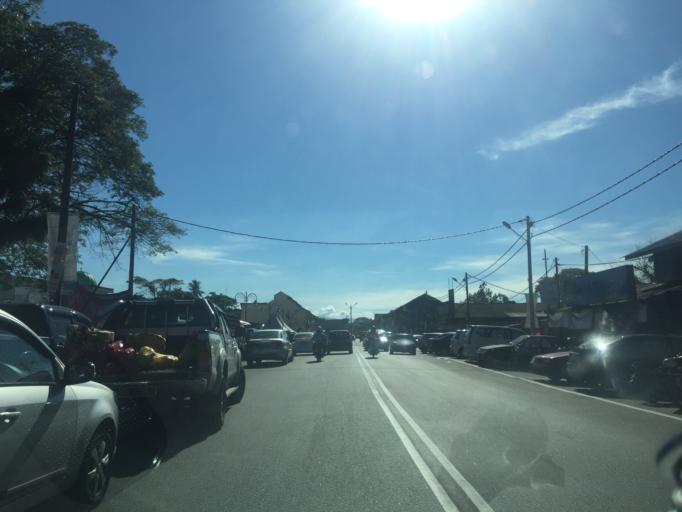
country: MY
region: Penang
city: Tasek Glugor
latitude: 5.5136
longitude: 100.5526
